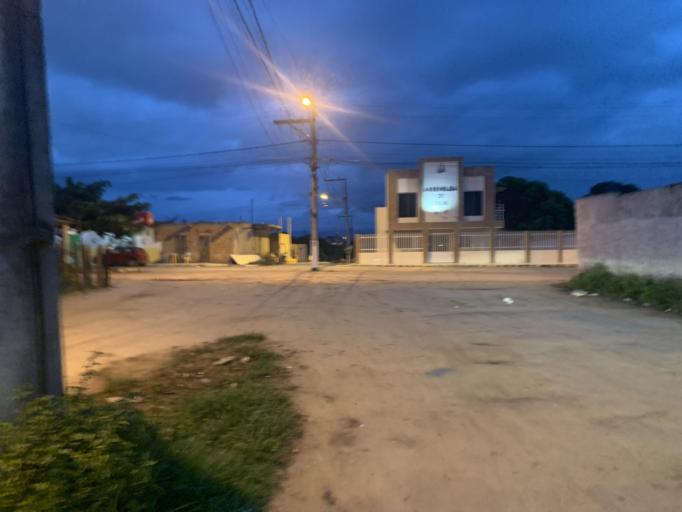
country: BR
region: Bahia
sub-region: Medeiros Neto
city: Medeiros Neto
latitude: -17.3887
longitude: -40.2334
